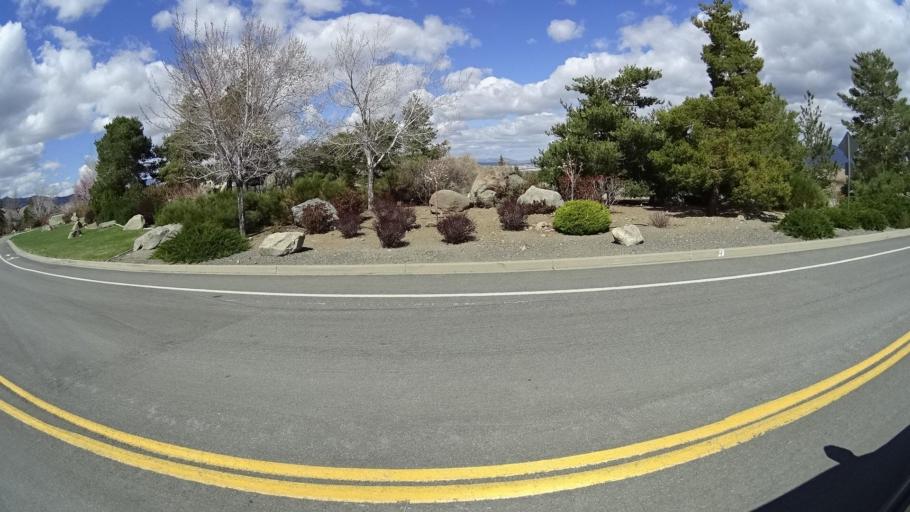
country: US
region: Nevada
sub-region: Washoe County
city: Reno
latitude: 39.4187
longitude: -119.7900
